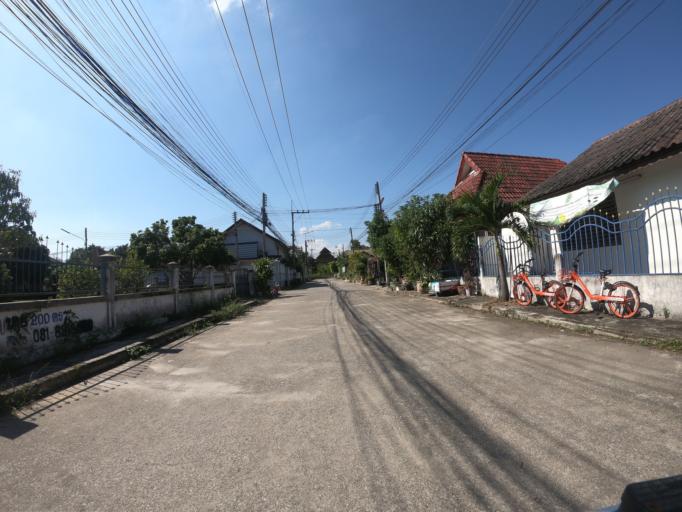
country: TH
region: Chiang Mai
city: Chiang Mai
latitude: 18.7441
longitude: 98.9728
